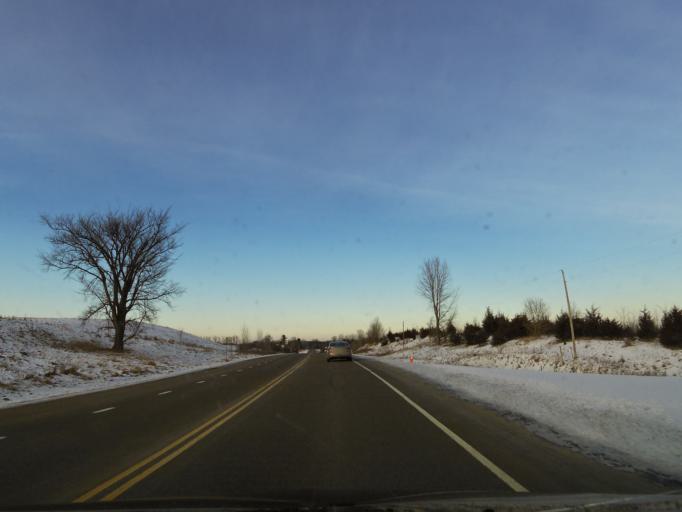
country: US
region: Wisconsin
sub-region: Polk County
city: Osceola
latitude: 45.3507
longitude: -92.7129
